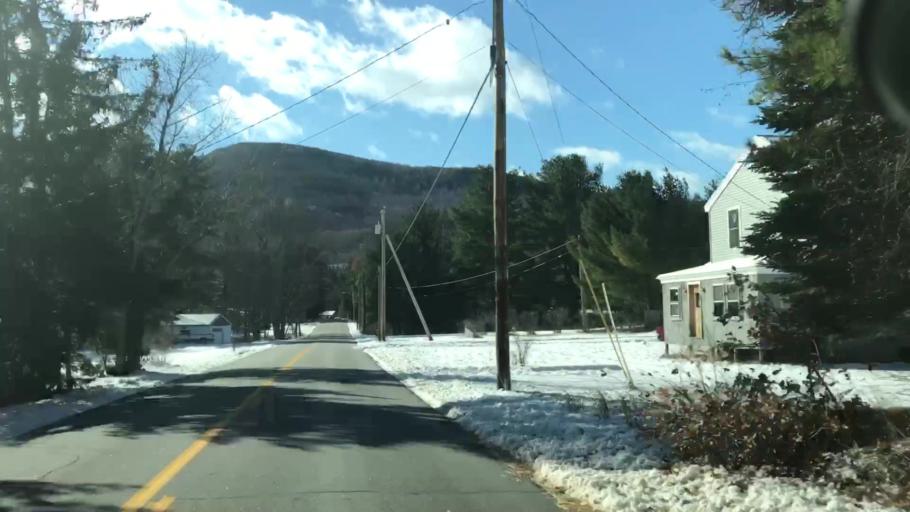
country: US
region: Maine
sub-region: Oxford County
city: Brownfield
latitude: 43.9362
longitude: -70.8925
